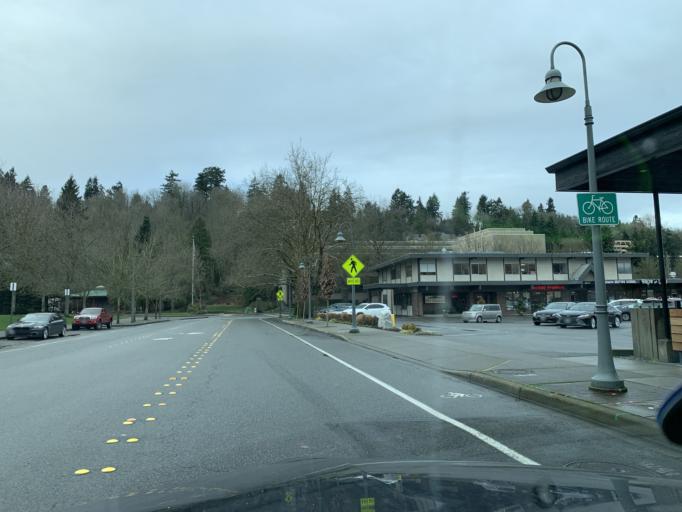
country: US
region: Washington
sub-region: King County
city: Mercer Island
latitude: 47.5819
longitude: -122.2339
